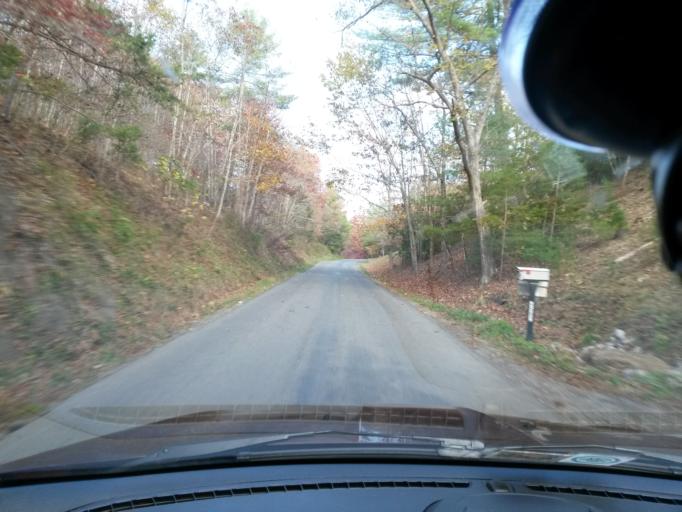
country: US
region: Virginia
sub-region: Alleghany County
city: Clifton Forge
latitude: 37.7994
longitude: -79.7505
